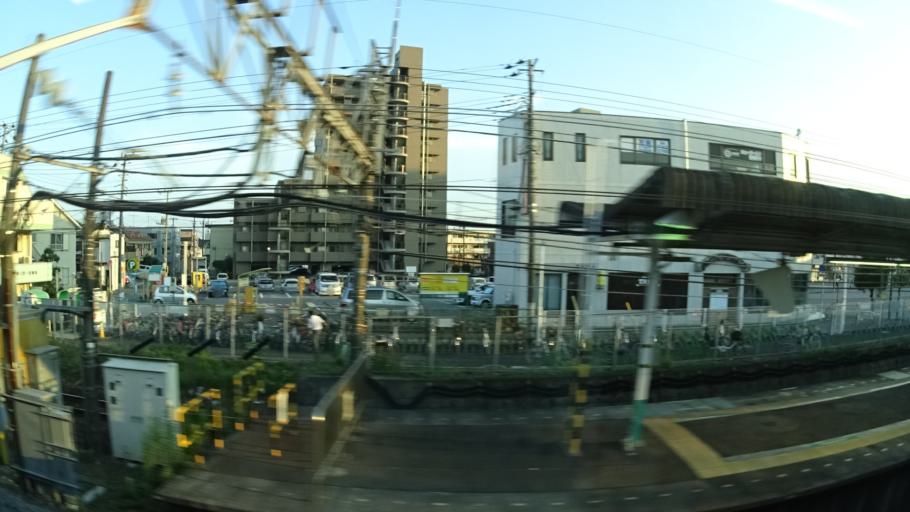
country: JP
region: Chiba
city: Abiko
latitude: 35.8756
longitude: 139.9894
